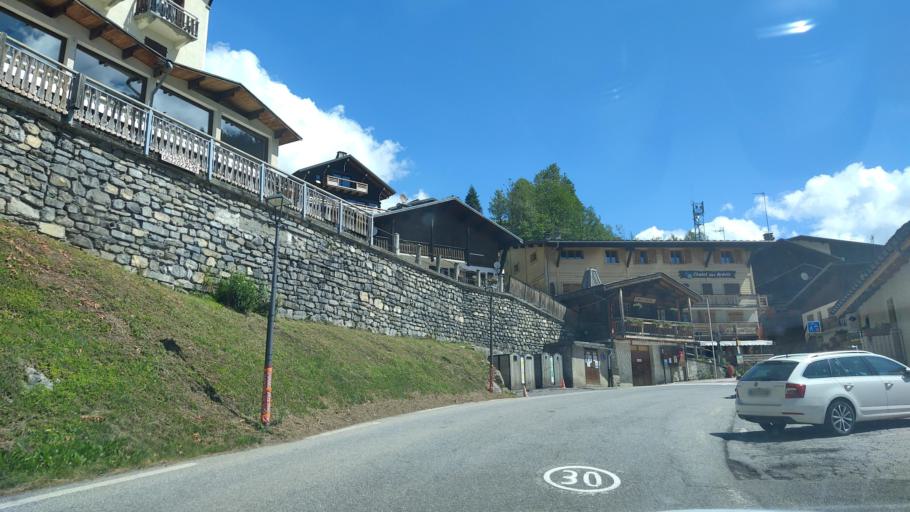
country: FR
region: Rhone-Alpes
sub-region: Departement de la Haute-Savoie
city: La Clusaz
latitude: 45.8624
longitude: 6.4944
